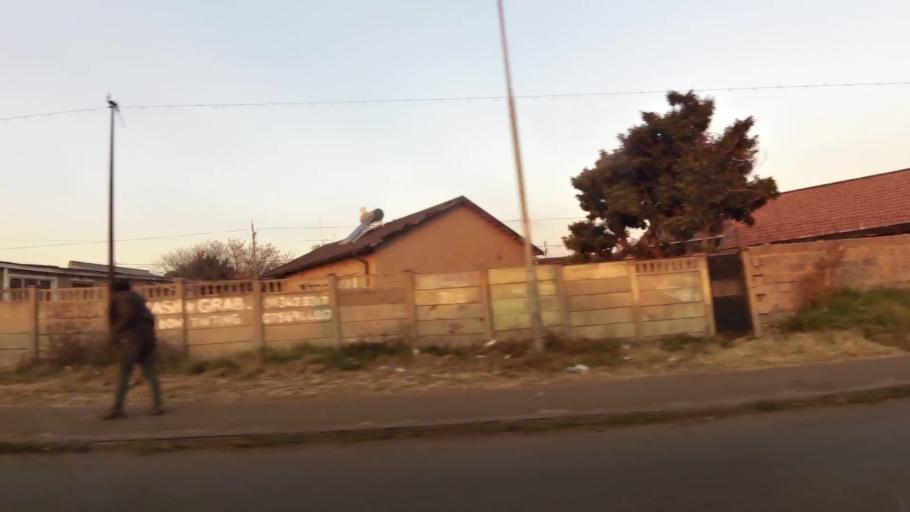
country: ZA
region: Gauteng
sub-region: City of Johannesburg Metropolitan Municipality
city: Soweto
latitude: -26.2859
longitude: 27.8912
